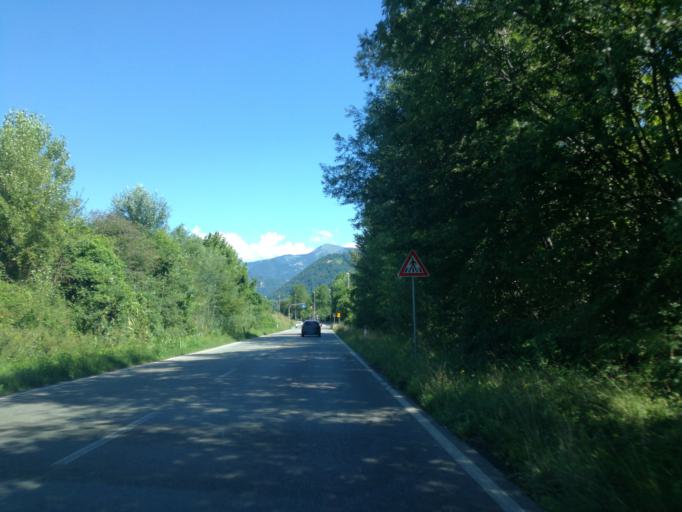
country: IT
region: Lombardy
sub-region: Provincia di Lecco
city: Imbersago
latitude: 45.7012
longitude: 9.4486
